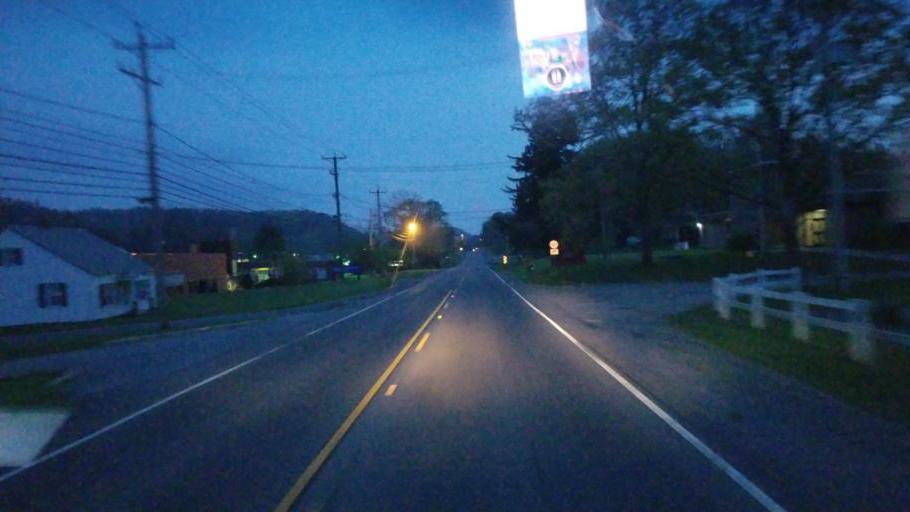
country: US
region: Virginia
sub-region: Smyth County
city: Marion
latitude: 36.8552
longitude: -81.4712
